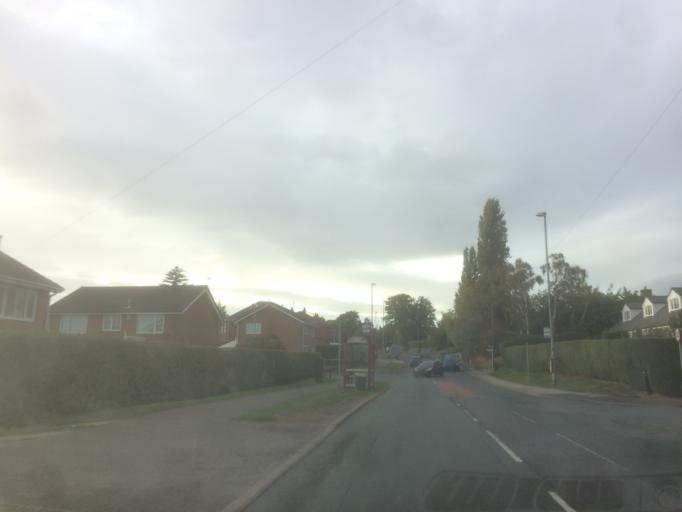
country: GB
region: England
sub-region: City and Borough of Wakefield
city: Pontefract
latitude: 53.7165
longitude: -1.3054
